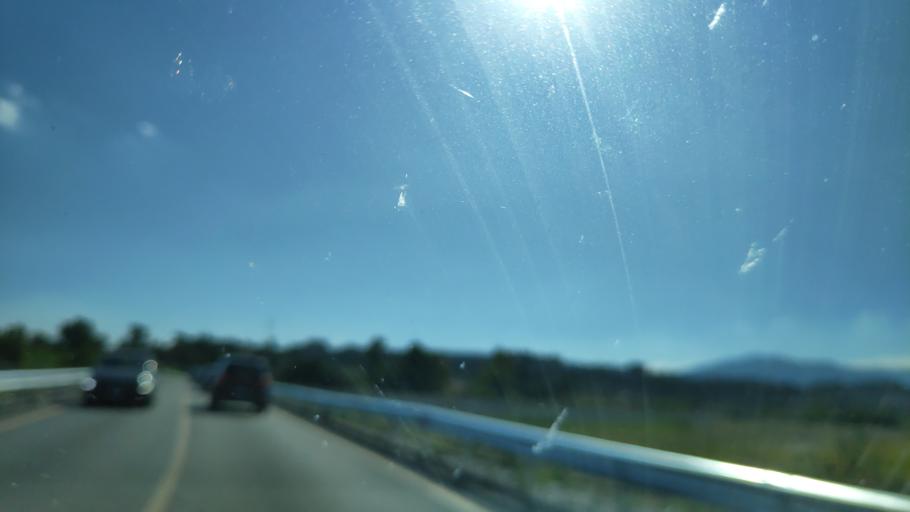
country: IT
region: Calabria
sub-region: Provincia di Reggio Calabria
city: Caulonia Marina
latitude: 38.3494
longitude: 16.4731
